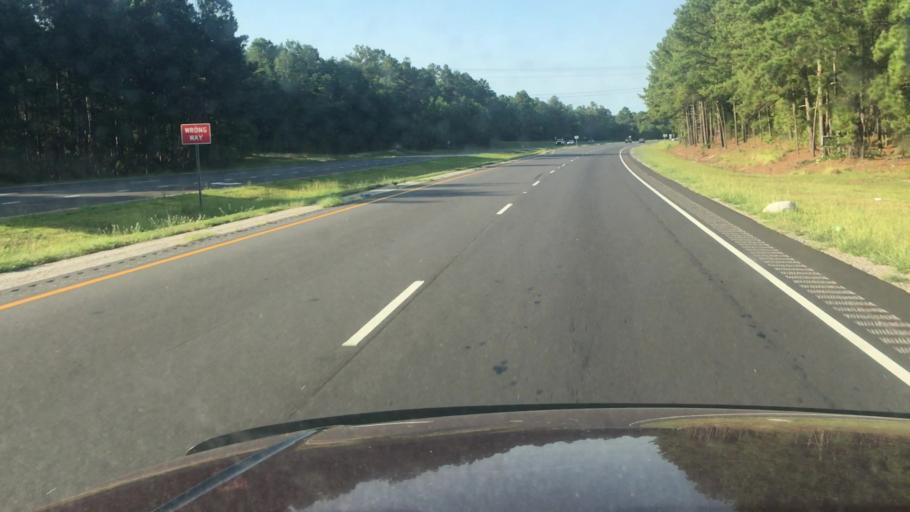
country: US
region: North Carolina
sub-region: Robeson County
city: Saint Pauls
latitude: 34.8575
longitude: -78.8498
